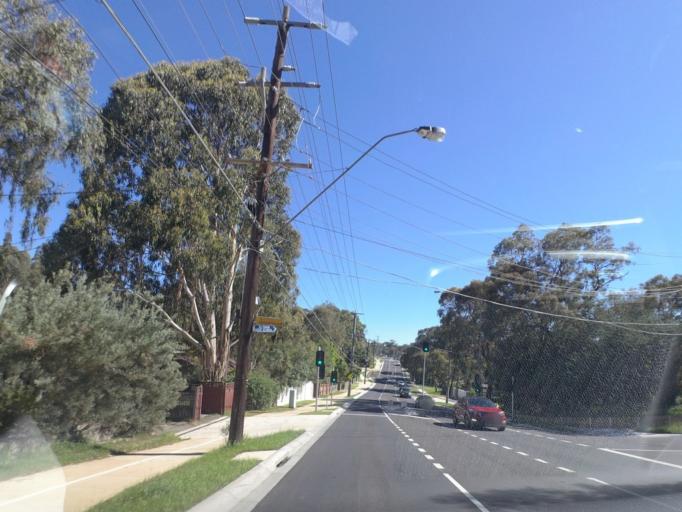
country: AU
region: Victoria
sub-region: Nillumbik
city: Eltham
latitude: -37.7235
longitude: 145.1364
